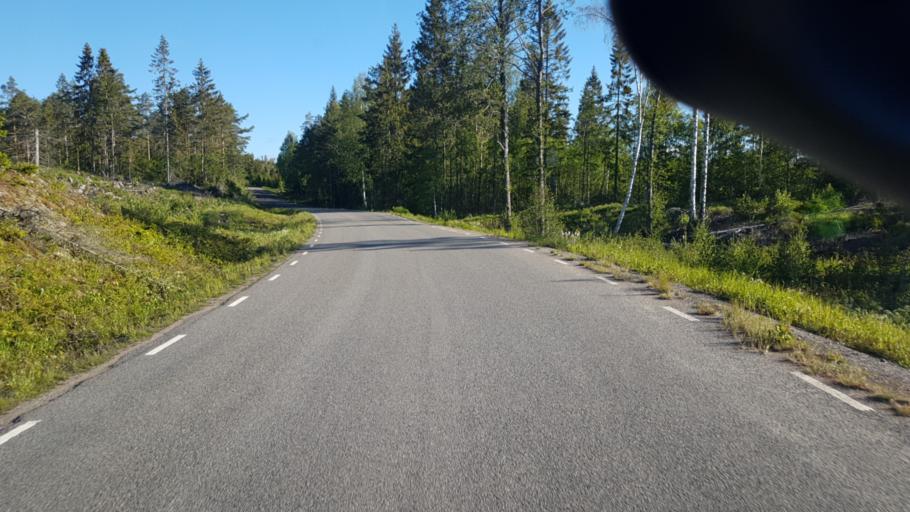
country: SE
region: Vaermland
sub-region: Arvika Kommun
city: Arvika
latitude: 59.5351
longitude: 12.3963
